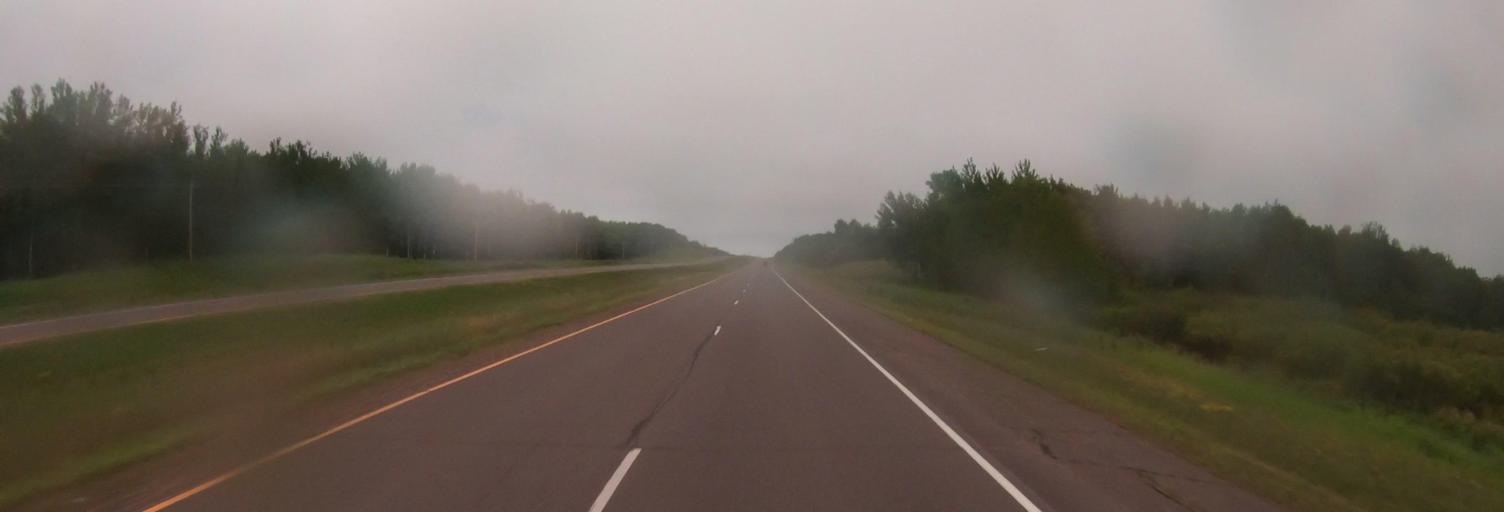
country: US
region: Minnesota
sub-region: Carlton County
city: Cloquet
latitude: 46.9268
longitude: -92.4716
